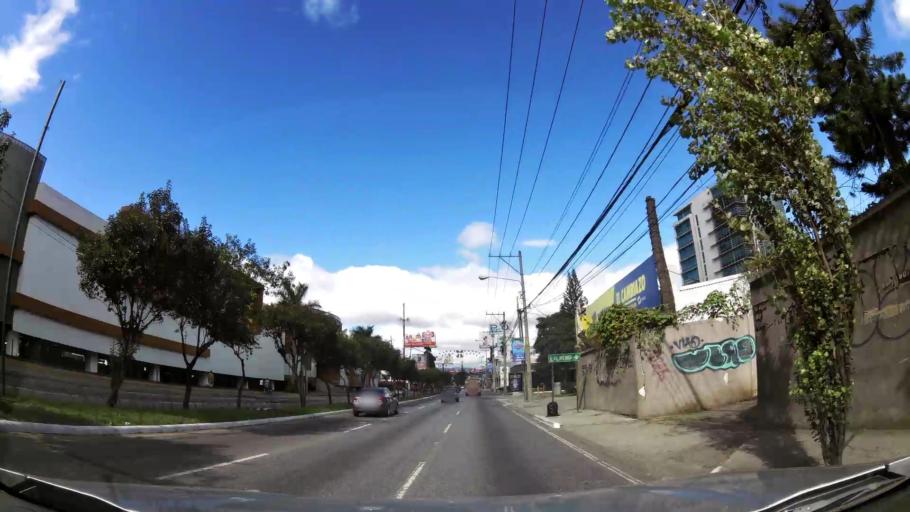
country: GT
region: Guatemala
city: Santa Catarina Pinula
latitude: 14.5929
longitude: -90.5125
